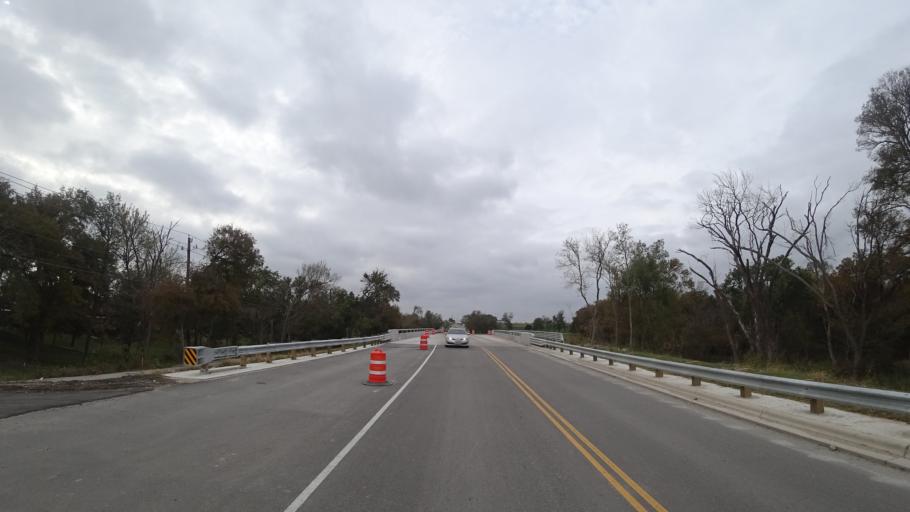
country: US
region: Texas
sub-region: Travis County
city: Pflugerville
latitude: 30.4257
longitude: -97.5755
